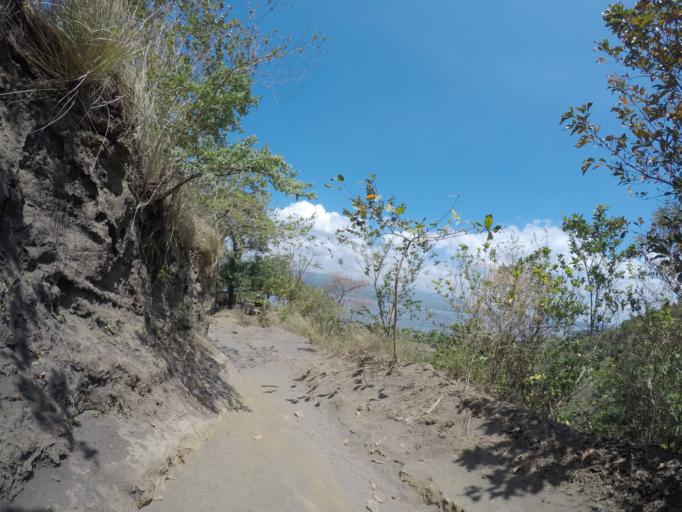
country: PH
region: Calabarzon
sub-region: Province of Batangas
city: Sampaloc
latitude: 14.0299
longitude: 121.0009
